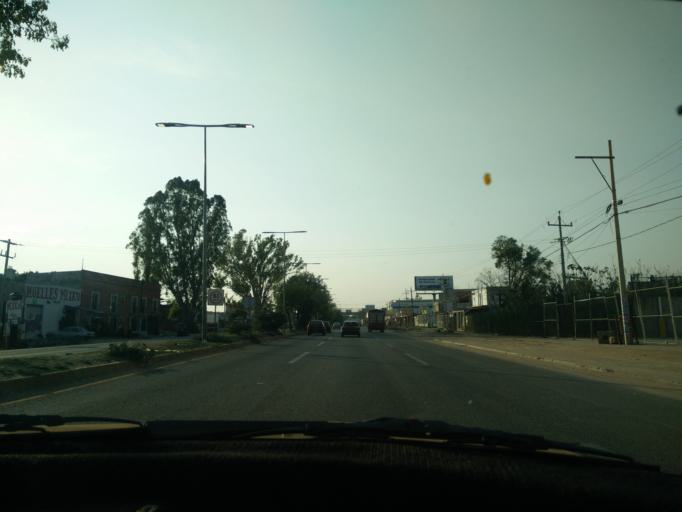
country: MX
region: Oaxaca
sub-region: Santa Maria Atzompa
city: Fraccionamiento Riberas de San Jeronimo
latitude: 17.1266
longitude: -96.7676
